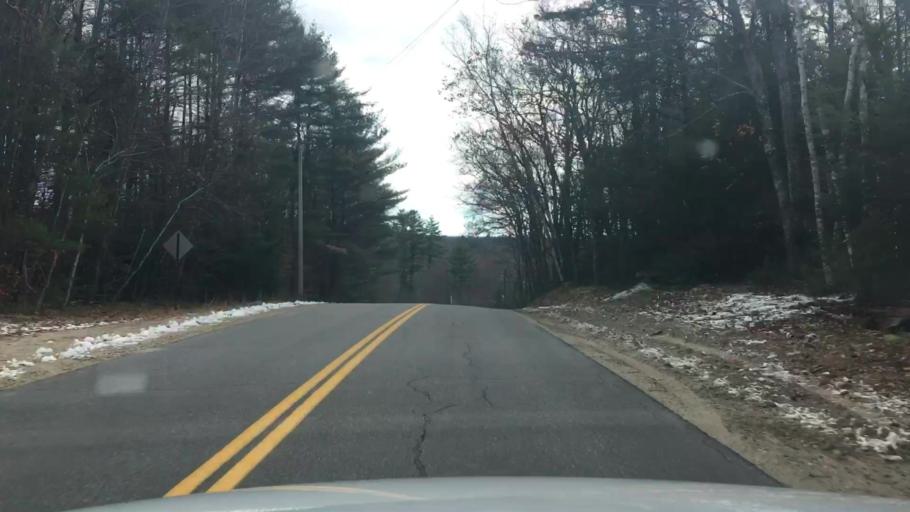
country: US
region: Maine
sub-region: Oxford County
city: Canton
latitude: 44.4912
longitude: -70.3280
